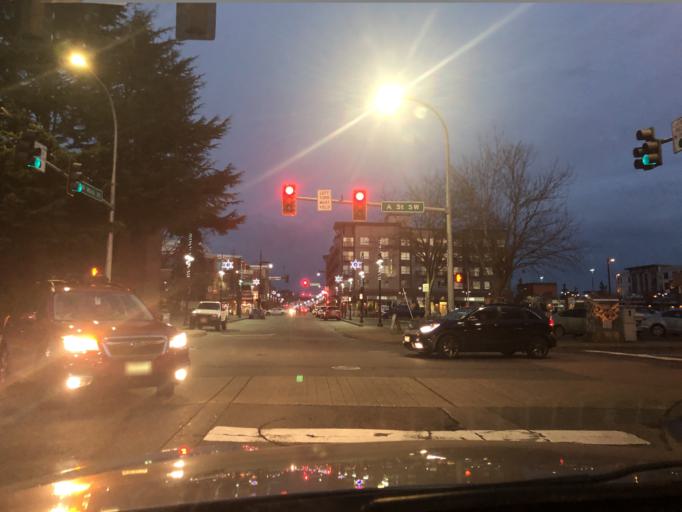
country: US
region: Washington
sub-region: King County
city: Auburn
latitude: 47.3074
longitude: -122.2312
